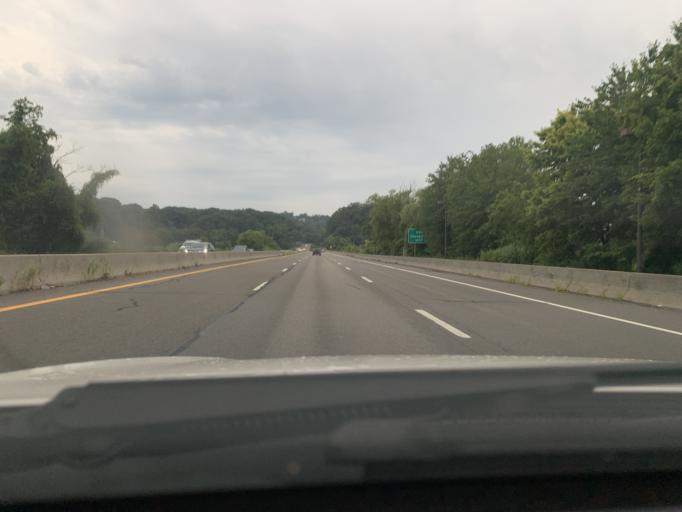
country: US
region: New York
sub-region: Westchester County
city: Croton-on-Hudson
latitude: 41.1901
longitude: -73.8784
